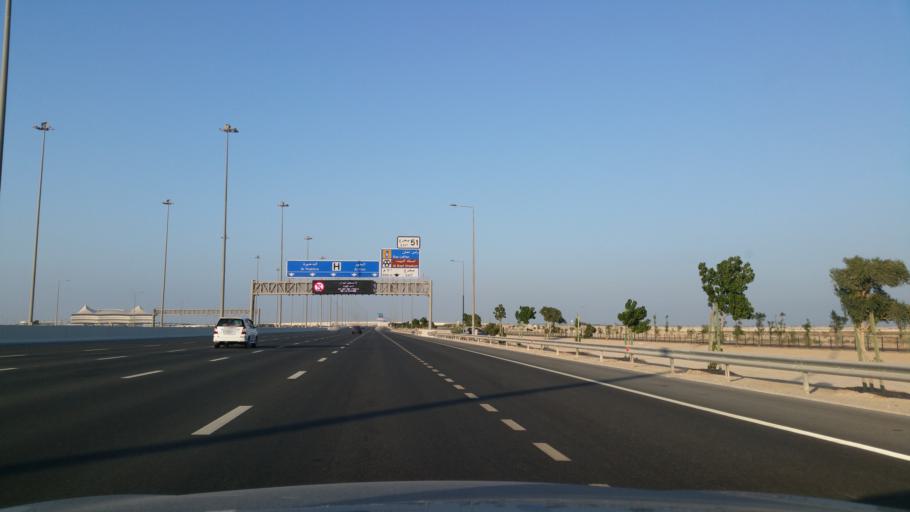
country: QA
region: Baladiyat az Za`ayin
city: Az Za`ayin
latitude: 25.6248
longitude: 51.4864
